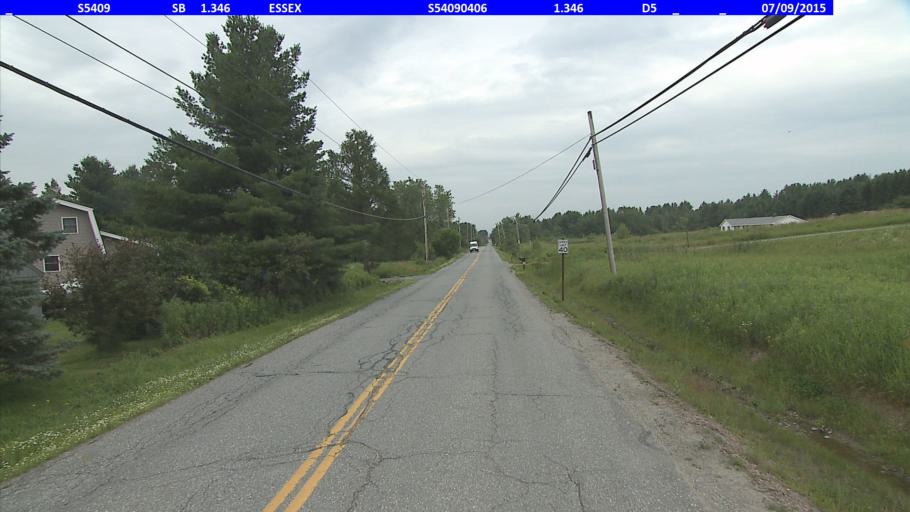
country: US
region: Vermont
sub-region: Chittenden County
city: Essex Junction
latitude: 44.5288
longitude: -73.0773
